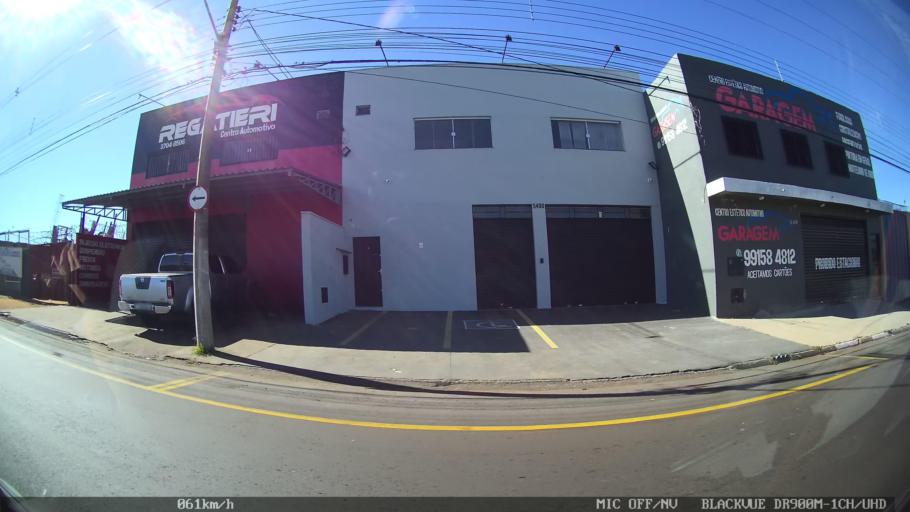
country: BR
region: Sao Paulo
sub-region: Franca
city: Franca
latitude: -20.5458
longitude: -47.3596
